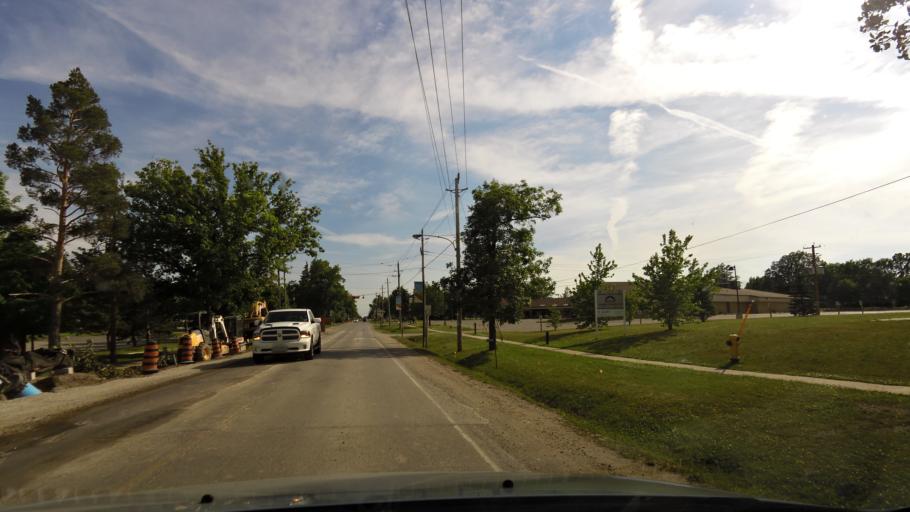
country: CA
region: Ontario
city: Brantford
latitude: 43.0722
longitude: -80.1158
